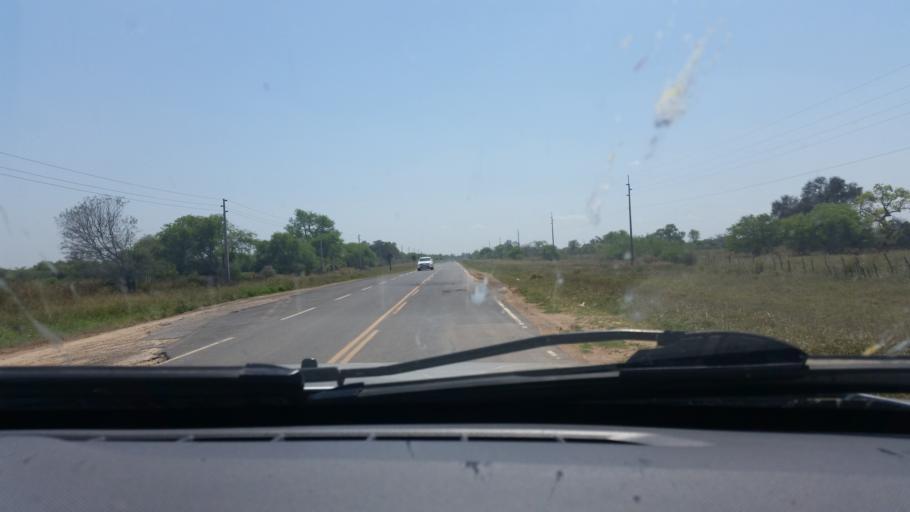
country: PY
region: Boqueron
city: Filadelfia
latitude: -22.4244
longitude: -60.0270
